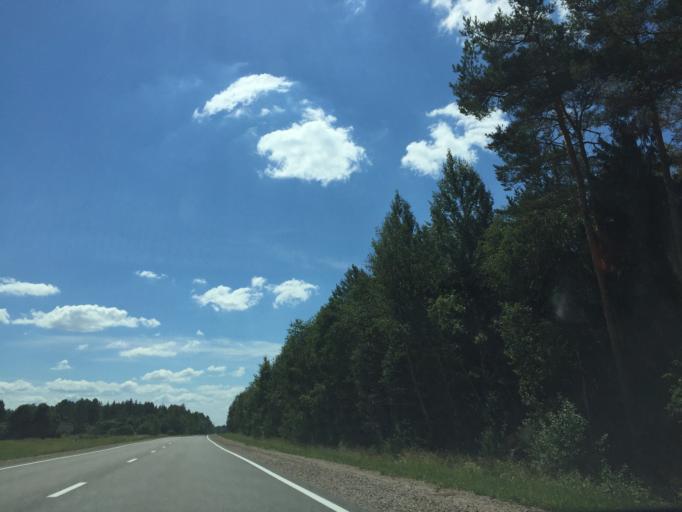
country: LV
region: Rezekne
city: Rezekne
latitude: 56.5147
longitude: 27.2707
